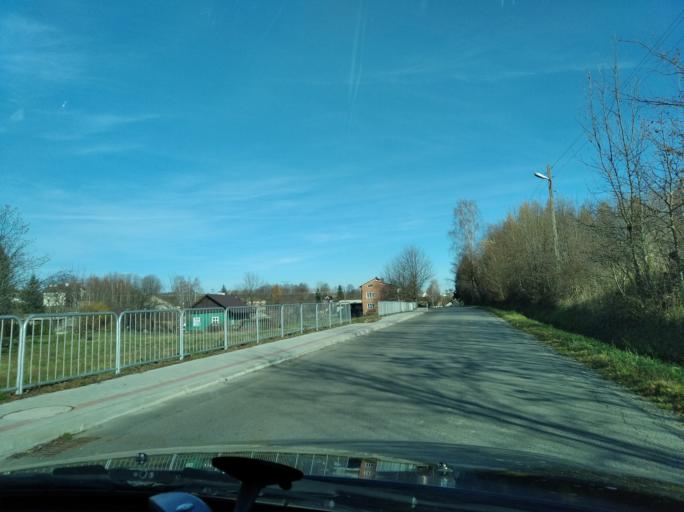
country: PL
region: Subcarpathian Voivodeship
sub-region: Powiat rzeszowski
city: Lutoryz
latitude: 49.9634
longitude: 21.8962
